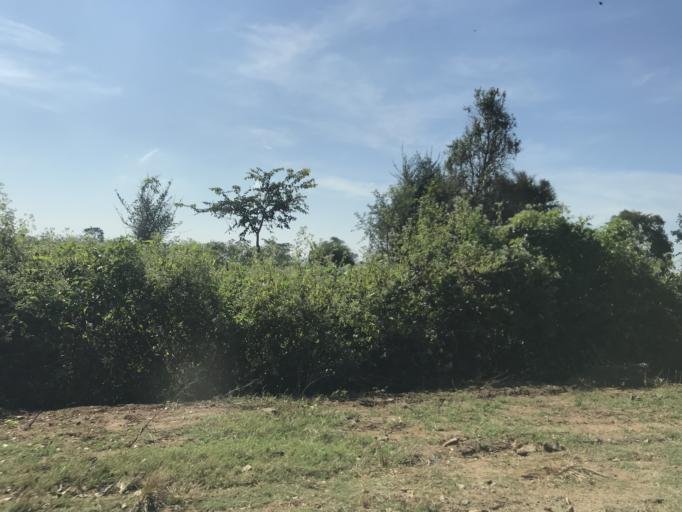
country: IN
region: Karnataka
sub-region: Mysore
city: Heggadadevankote
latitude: 12.0465
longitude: 76.3376
